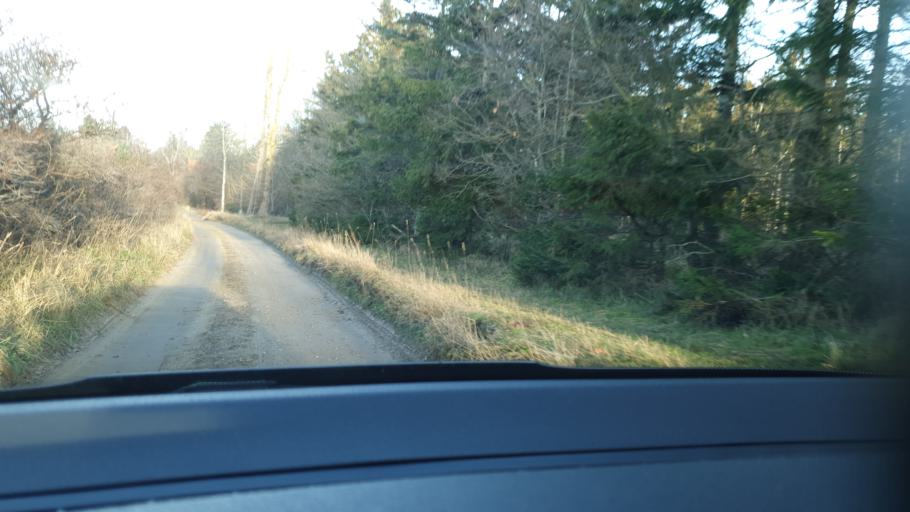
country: DK
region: Zealand
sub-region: Odsherred Kommune
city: Hojby
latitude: 55.9305
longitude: 11.6224
